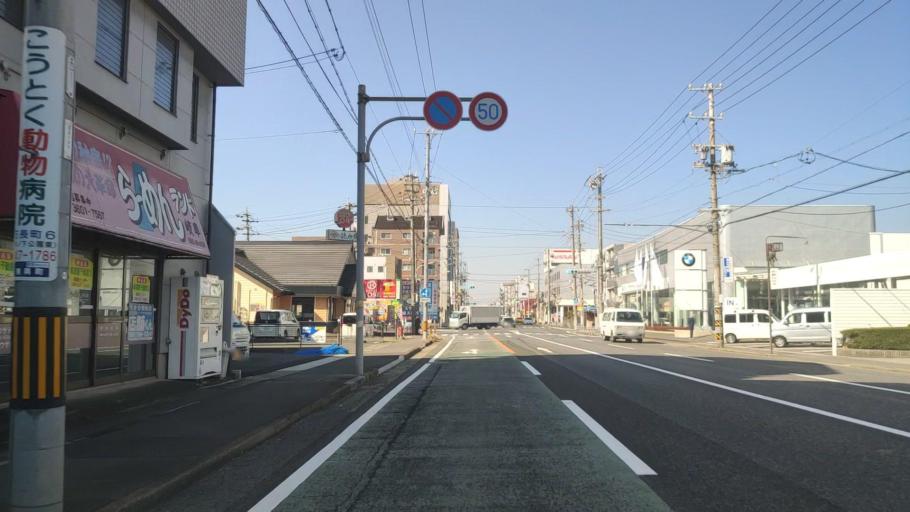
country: JP
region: Gifu
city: Gifu-shi
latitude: 35.4165
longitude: 136.7828
